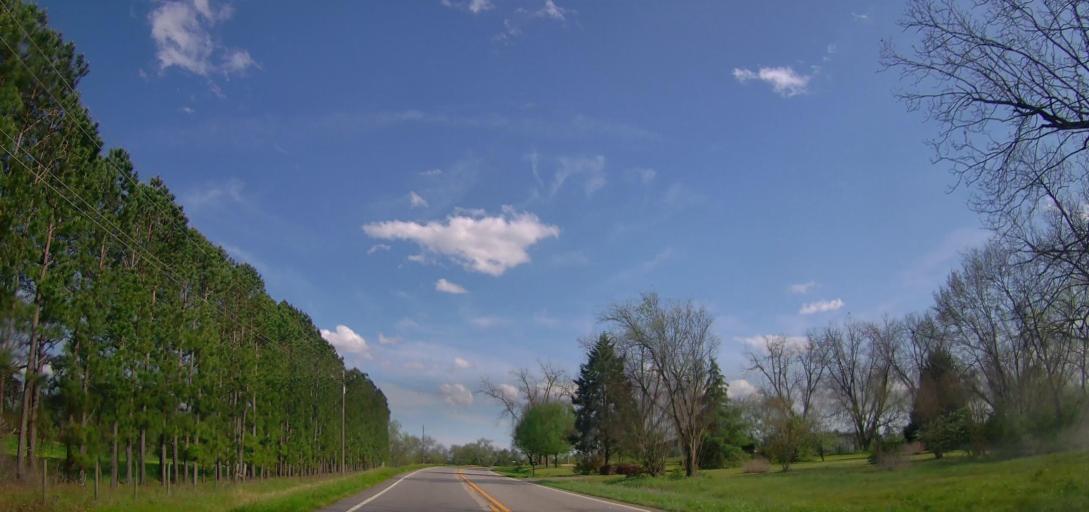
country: US
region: Georgia
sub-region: Baldwin County
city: Hardwick
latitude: 33.0749
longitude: -83.1382
